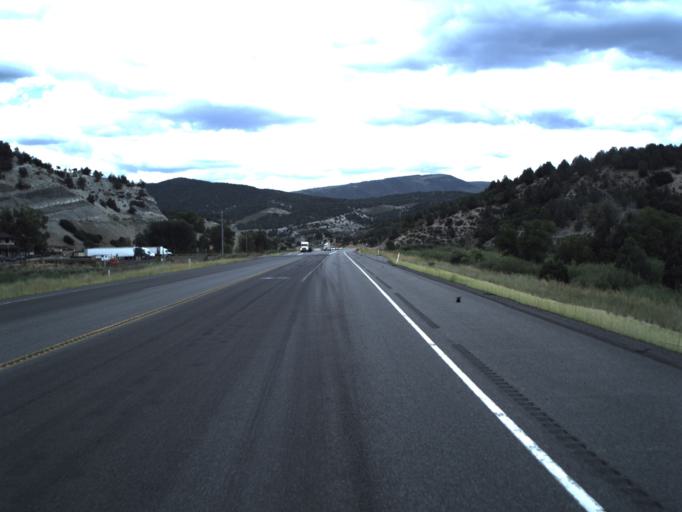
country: US
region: Utah
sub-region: Sanpete County
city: Fairview
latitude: 39.9509
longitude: -111.2212
